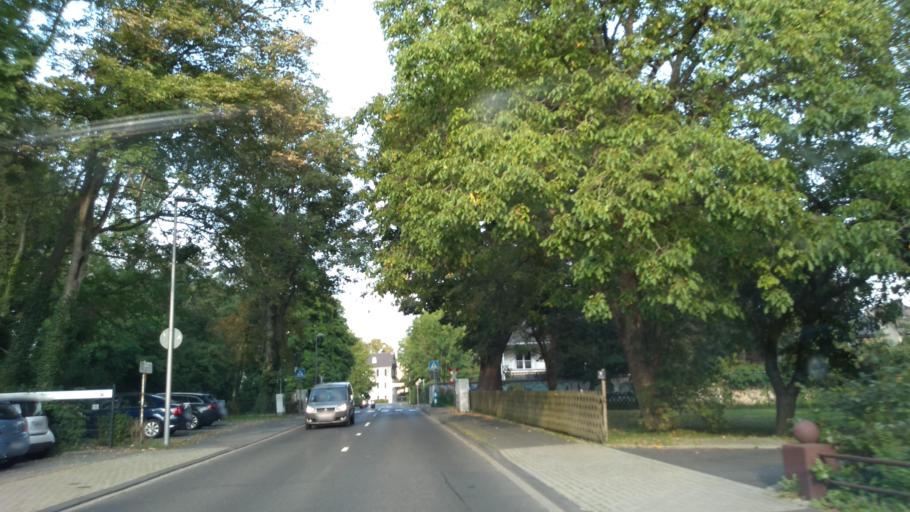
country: DE
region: North Rhine-Westphalia
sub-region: Regierungsbezirk Koln
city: Siegburg
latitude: 50.7936
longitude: 7.2116
